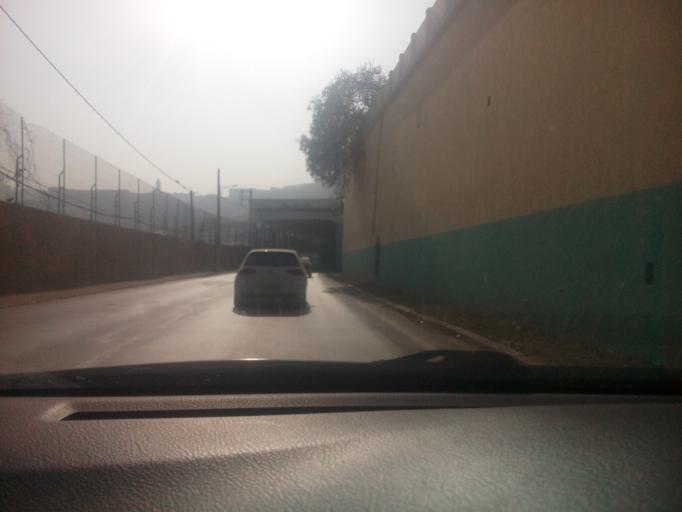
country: DZ
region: Oran
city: Oran
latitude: 35.7120
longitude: -0.6569
